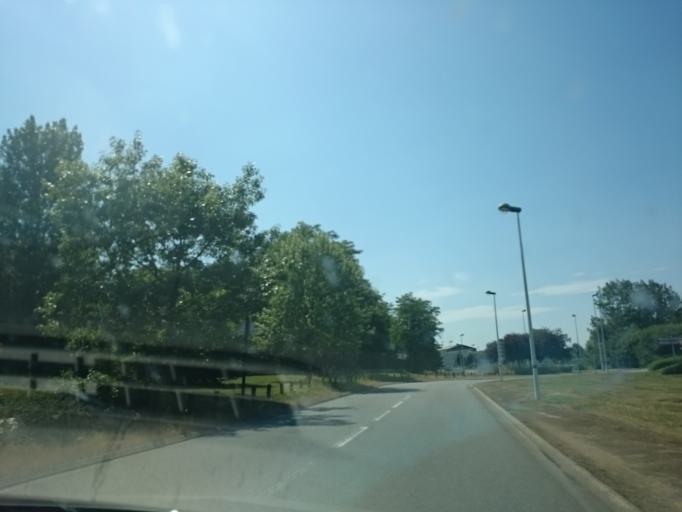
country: FR
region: Pays de la Loire
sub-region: Departement de la Loire-Atlantique
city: Indre
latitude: 47.2038
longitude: -1.6748
